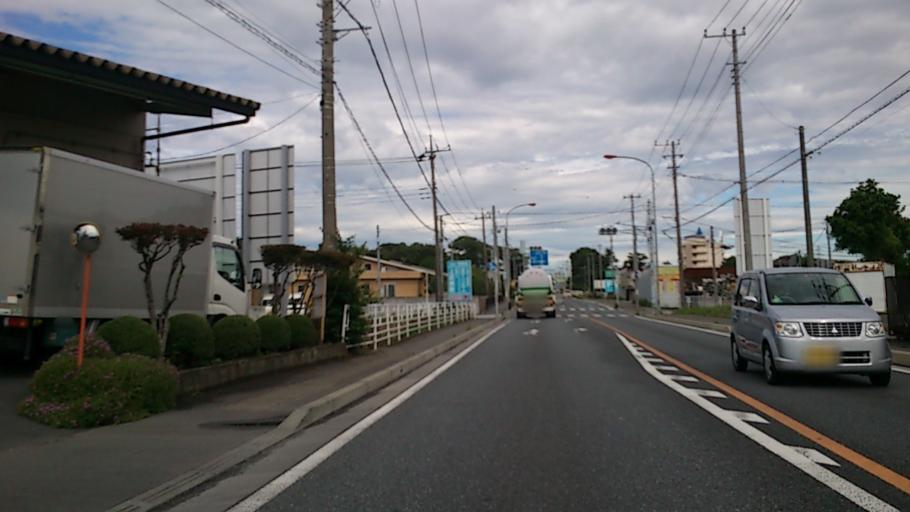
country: JP
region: Saitama
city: Honjo
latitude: 36.2504
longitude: 139.1775
